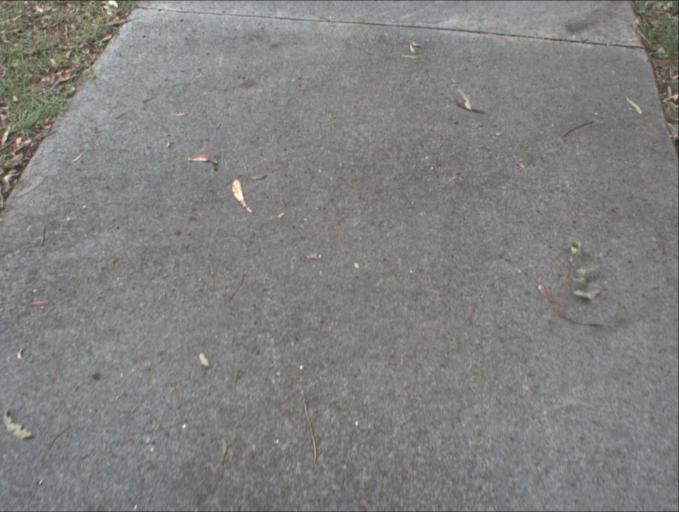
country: AU
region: Queensland
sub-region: Brisbane
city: Sunnybank Hills
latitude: -27.6606
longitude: 153.0516
